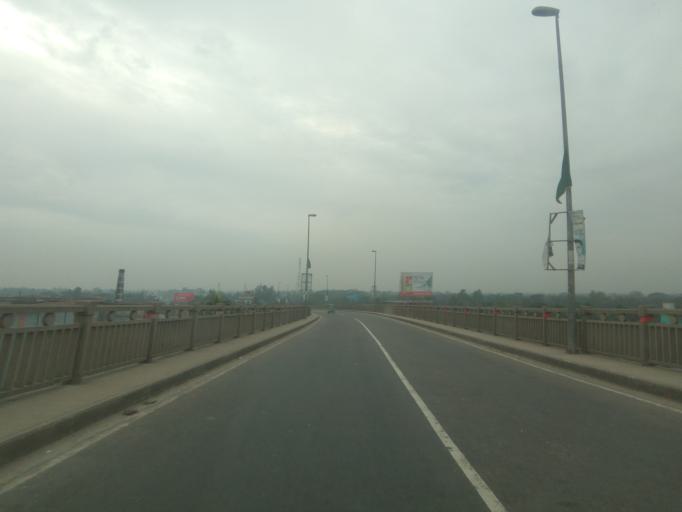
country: BD
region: Dhaka
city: Narayanganj
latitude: 23.5670
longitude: 90.5109
